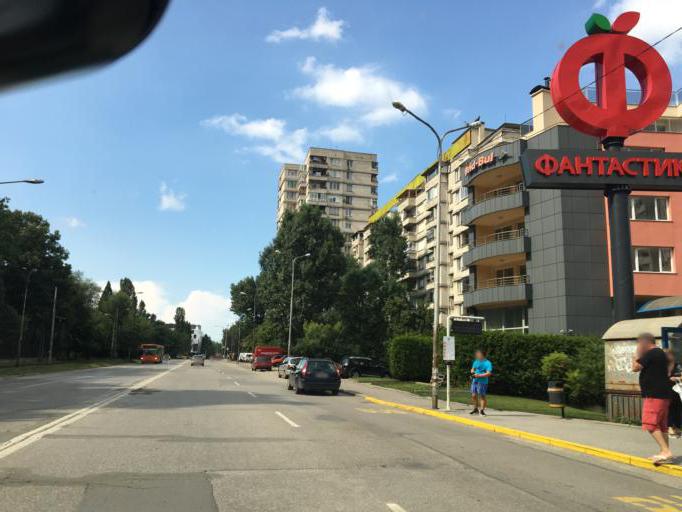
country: BG
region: Sofia-Capital
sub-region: Stolichna Obshtina
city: Sofia
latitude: 42.6537
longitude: 23.3597
